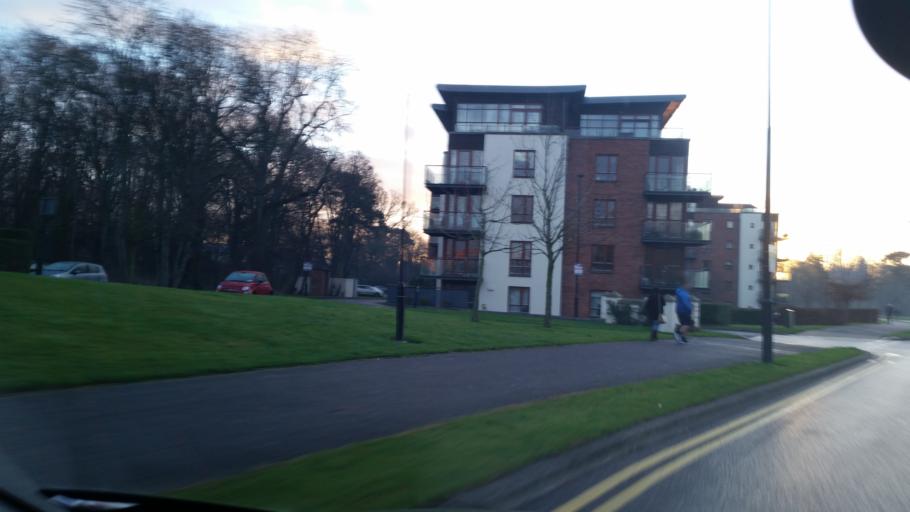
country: IE
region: Leinster
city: Beaumont
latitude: 53.4052
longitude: -6.2477
